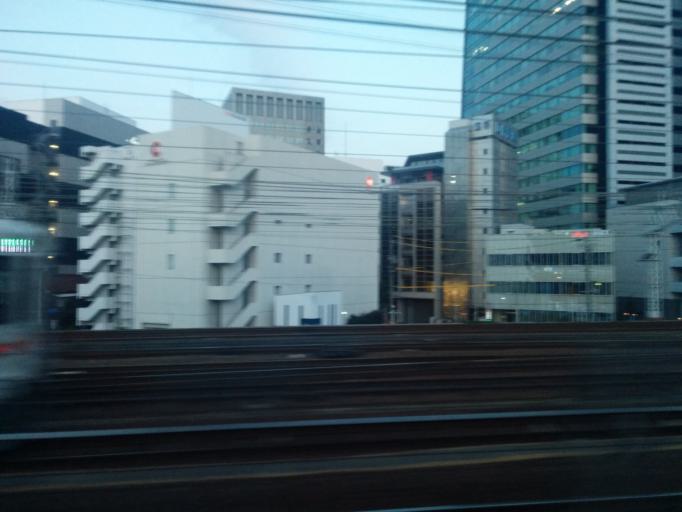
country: JP
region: Aichi
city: Nagoya-shi
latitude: 35.1758
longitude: 136.8808
